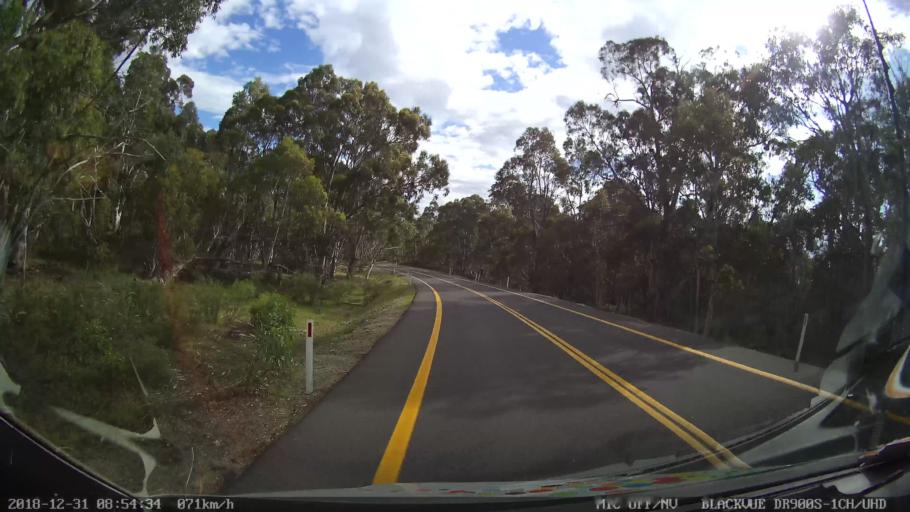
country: AU
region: New South Wales
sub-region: Snowy River
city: Jindabyne
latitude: -36.3532
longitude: 148.5628
